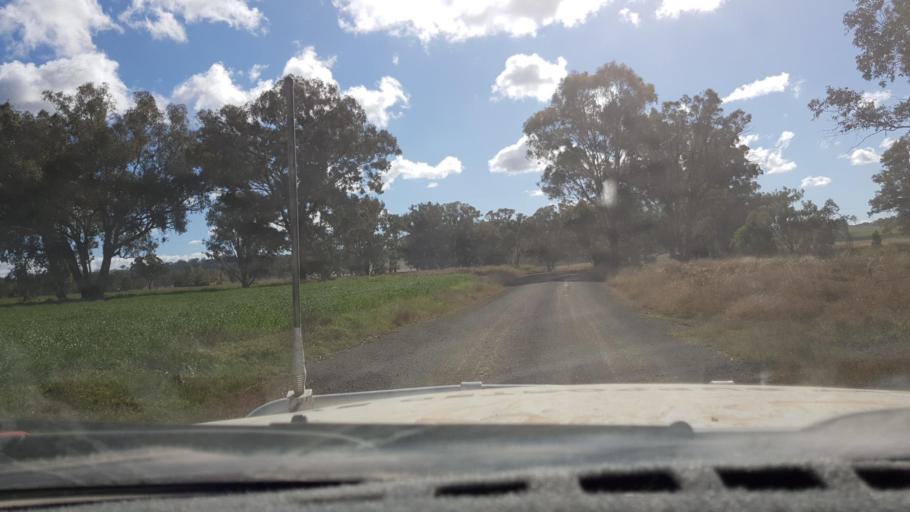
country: AU
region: New South Wales
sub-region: Narrabri
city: Blair Athol
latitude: -30.5753
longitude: 150.4715
